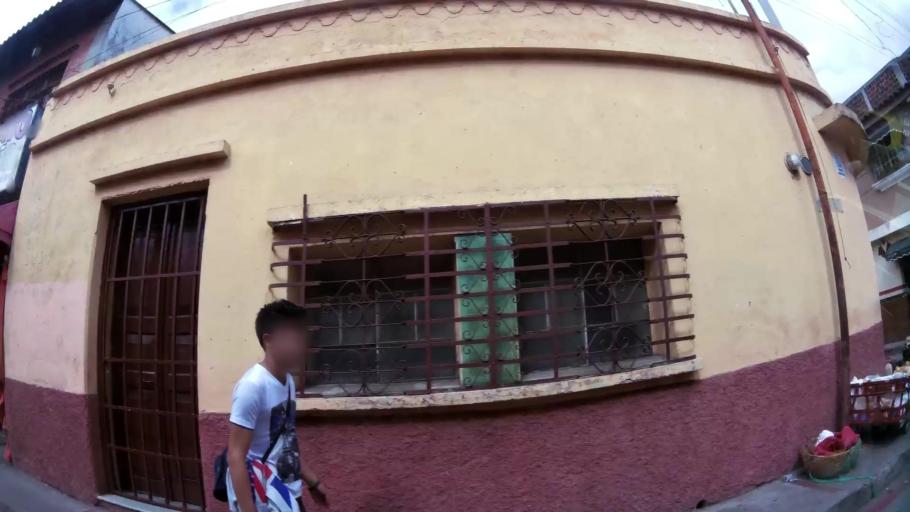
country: GT
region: Guatemala
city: Mixco
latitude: 14.6313
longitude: -90.6070
